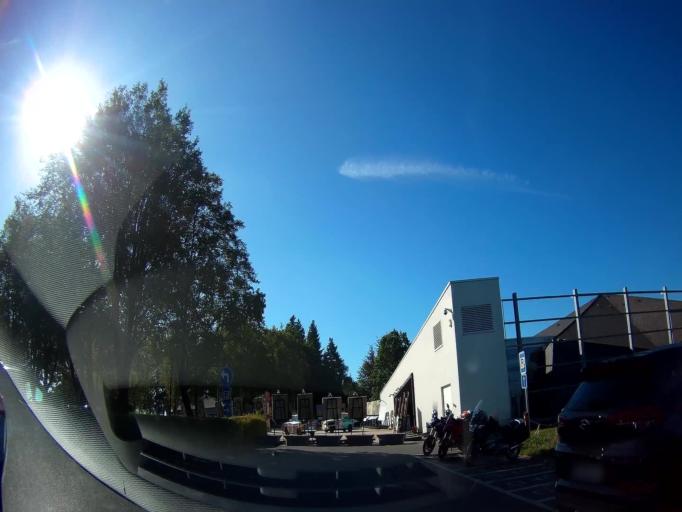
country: BE
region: Wallonia
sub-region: Province du Luxembourg
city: Bastogne
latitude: 50.0113
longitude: 5.7397
